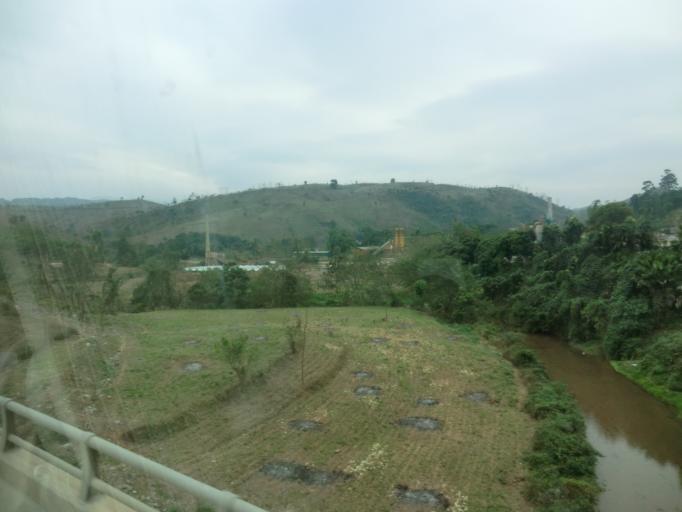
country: VN
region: Yen Bai
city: Thi Tran Yen The
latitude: 21.9511
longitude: 104.5789
